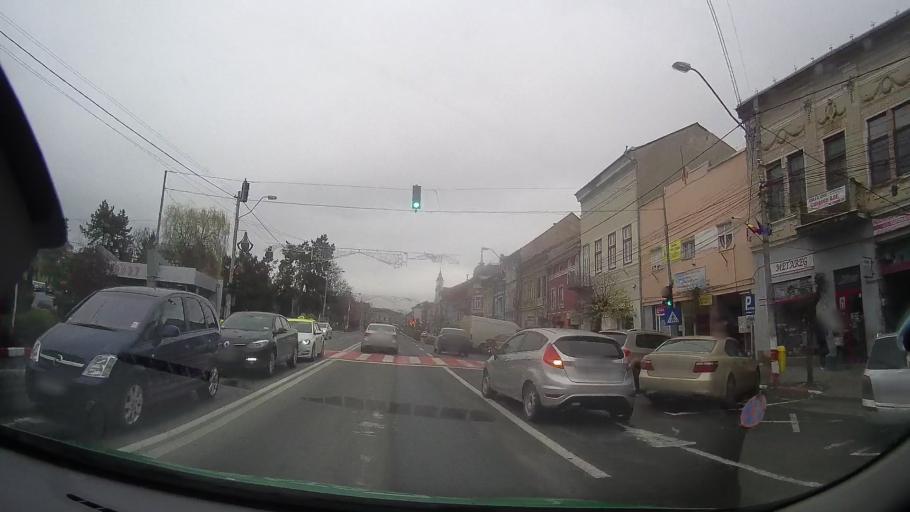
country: RO
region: Mures
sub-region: Municipiul Reghin
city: Reghin
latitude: 46.7802
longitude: 24.7005
